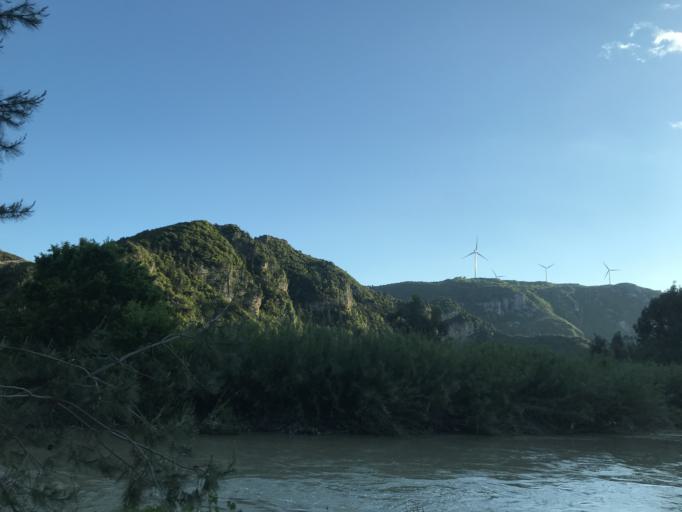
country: TR
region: Hatay
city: Buyukcat
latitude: 36.0791
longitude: 36.0400
